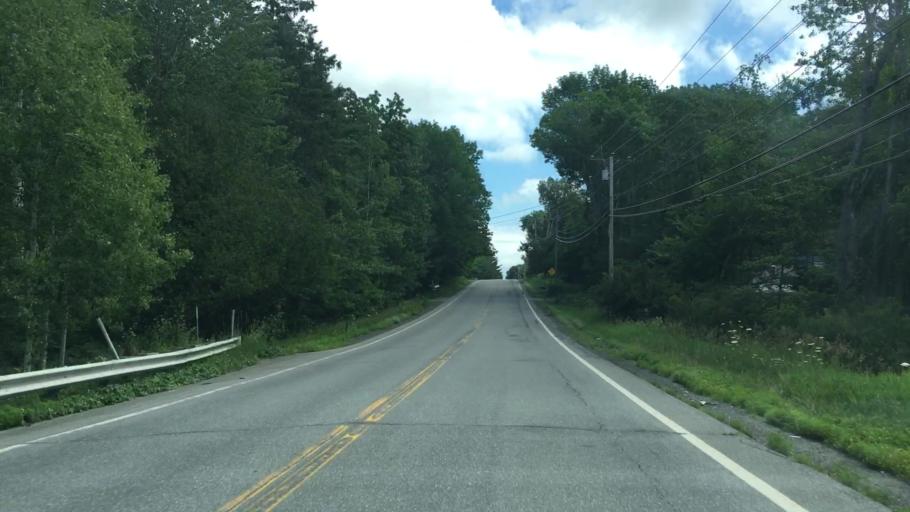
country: US
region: Maine
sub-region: Penobscot County
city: Hermon
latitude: 44.8065
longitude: -68.9429
